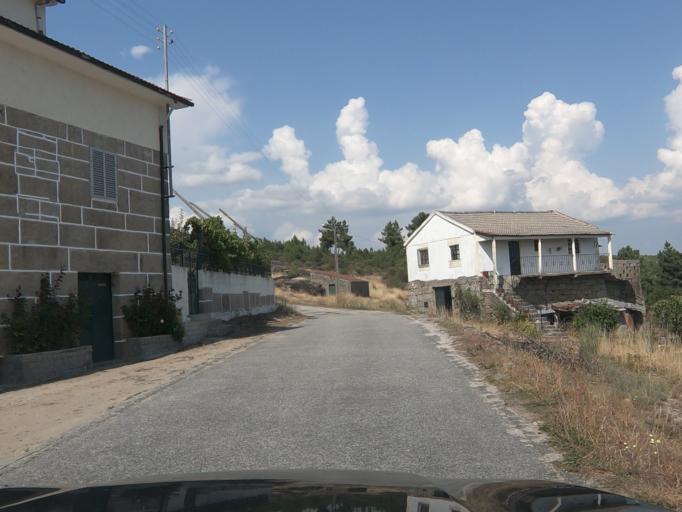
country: PT
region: Vila Real
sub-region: Sabrosa
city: Sabrosa
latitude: 41.3039
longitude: -7.5948
